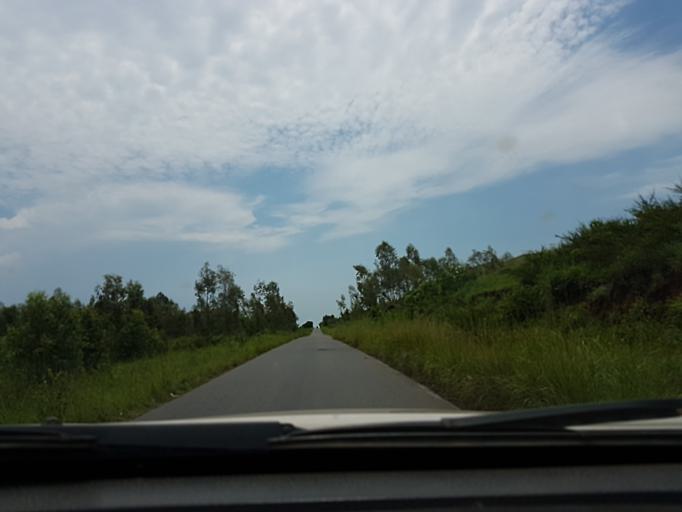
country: CD
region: South Kivu
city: Uvira
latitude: -3.2537
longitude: 29.1613
